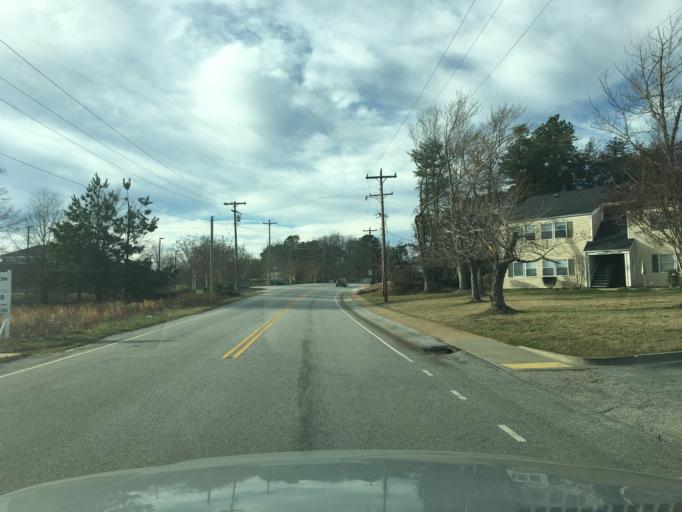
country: US
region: South Carolina
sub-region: Greenville County
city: Greer
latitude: 34.9390
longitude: -82.2454
